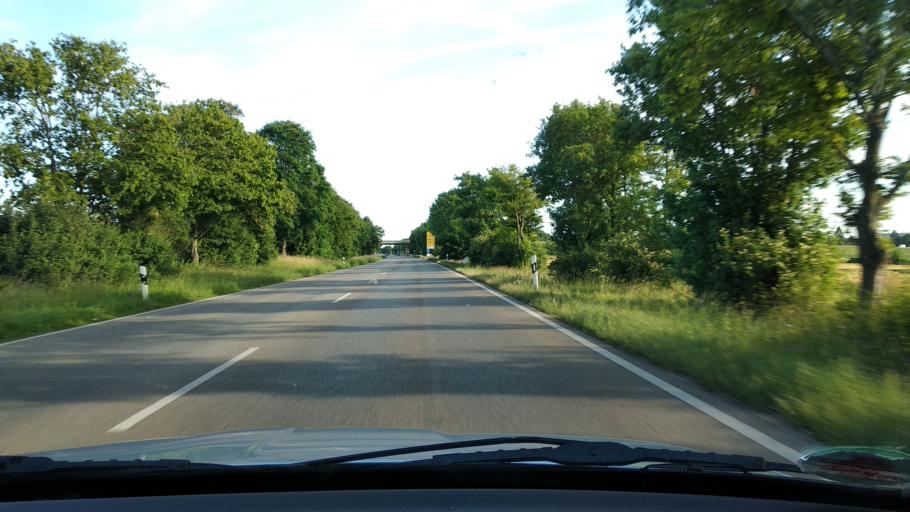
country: DE
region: Bavaria
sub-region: Swabia
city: Illertissen
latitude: 48.2111
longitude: 10.1024
